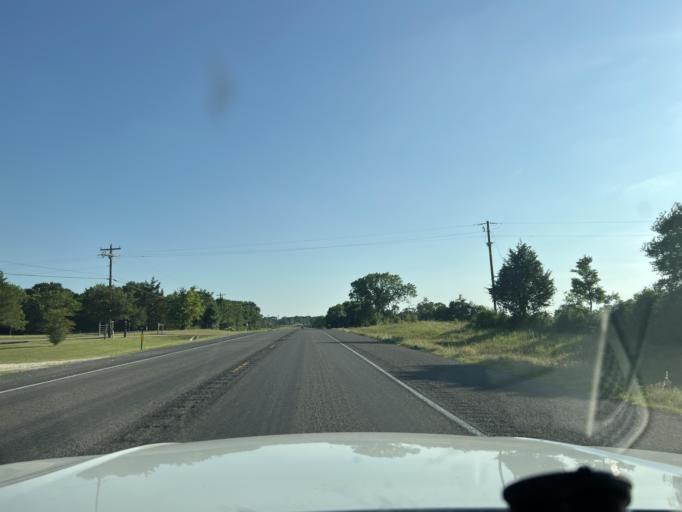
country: US
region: Texas
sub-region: Washington County
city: Brenham
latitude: 30.2258
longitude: -96.2969
